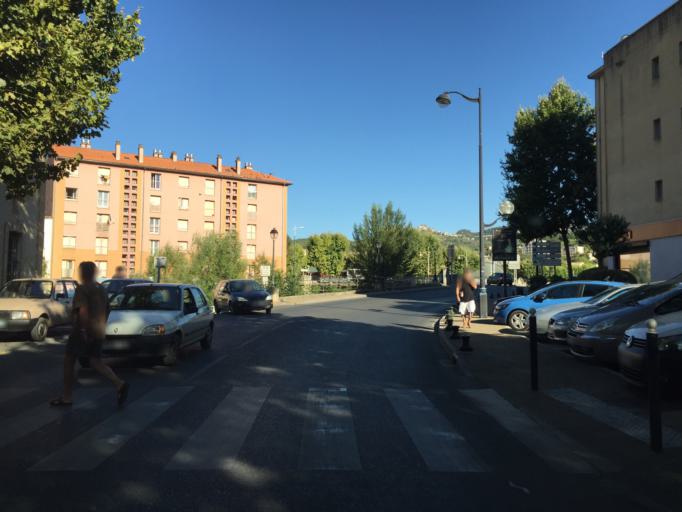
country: FR
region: Provence-Alpes-Cote d'Azur
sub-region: Departement du Vaucluse
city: Apt
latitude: 43.8768
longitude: 5.3991
